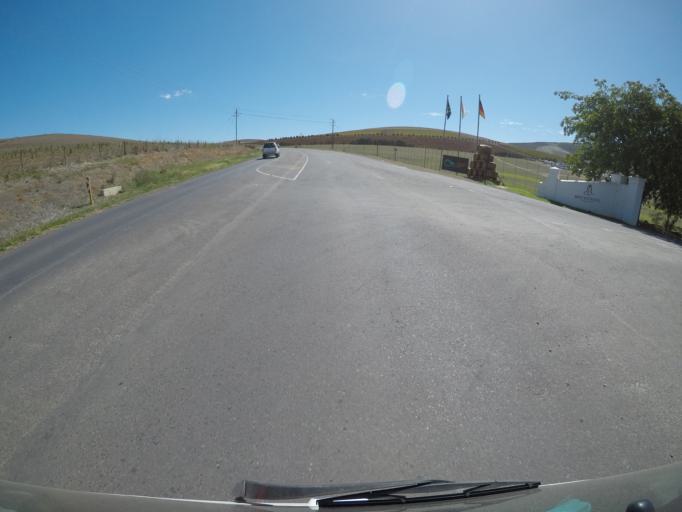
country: ZA
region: Western Cape
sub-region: City of Cape Town
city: Kraaifontein
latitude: -33.8027
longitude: 18.6194
